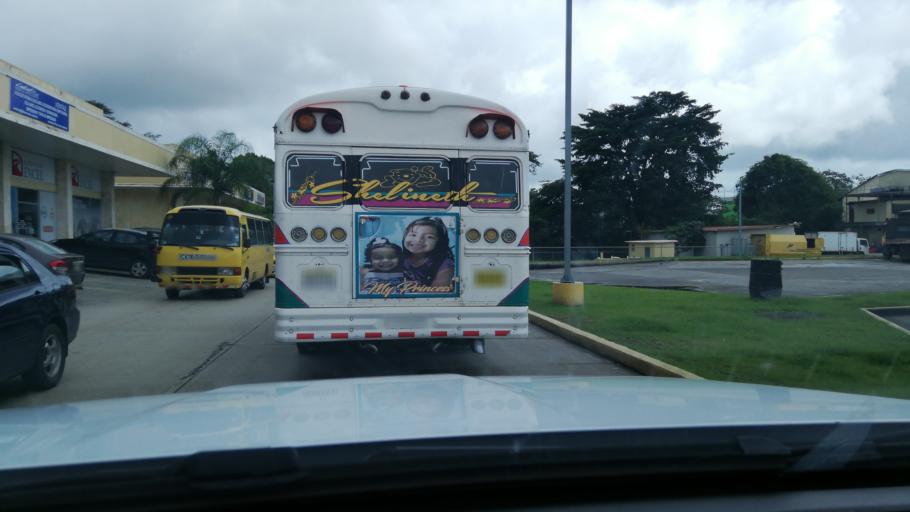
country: PA
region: Panama
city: Tocumen
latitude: 9.1052
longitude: -79.3698
